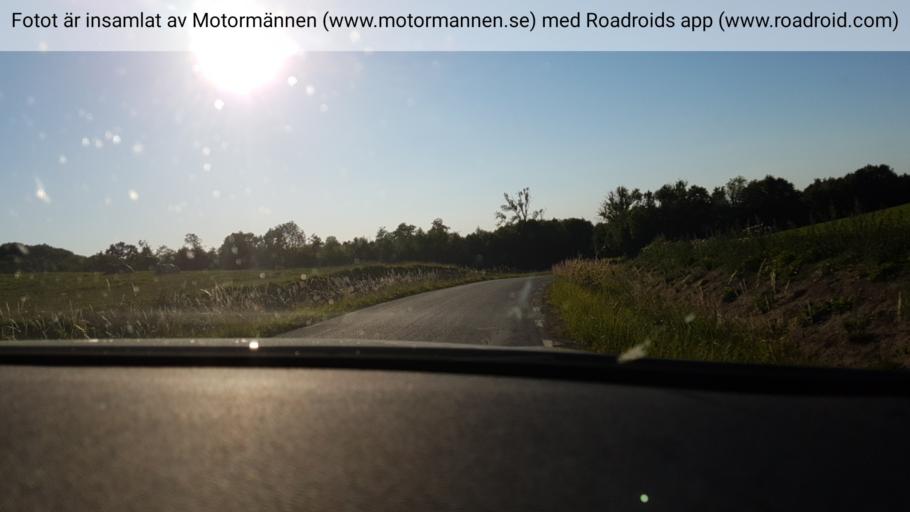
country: SE
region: Vaestra Goetaland
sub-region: Falkopings Kommun
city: Akarp
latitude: 58.1889
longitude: 13.7415
